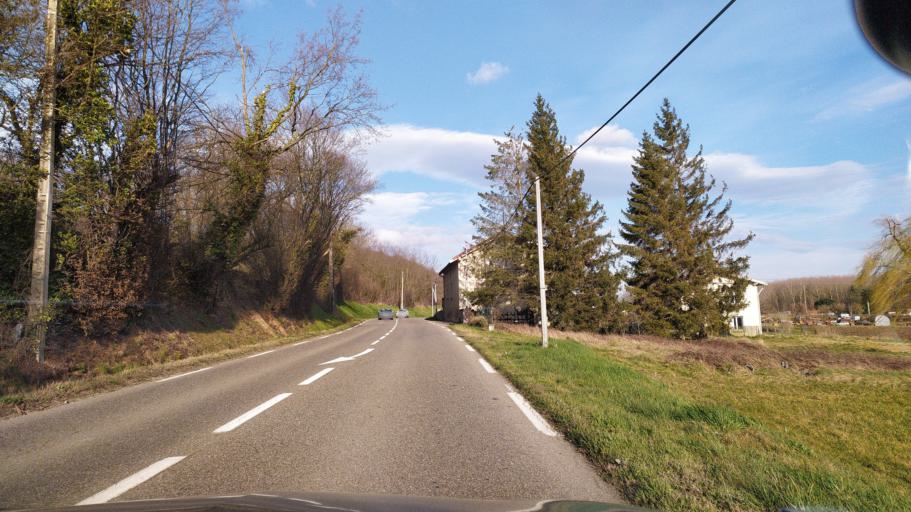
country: FR
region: Rhone-Alpes
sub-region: Departement de l'Isere
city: Serpaize
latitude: 45.5497
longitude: 4.9323
